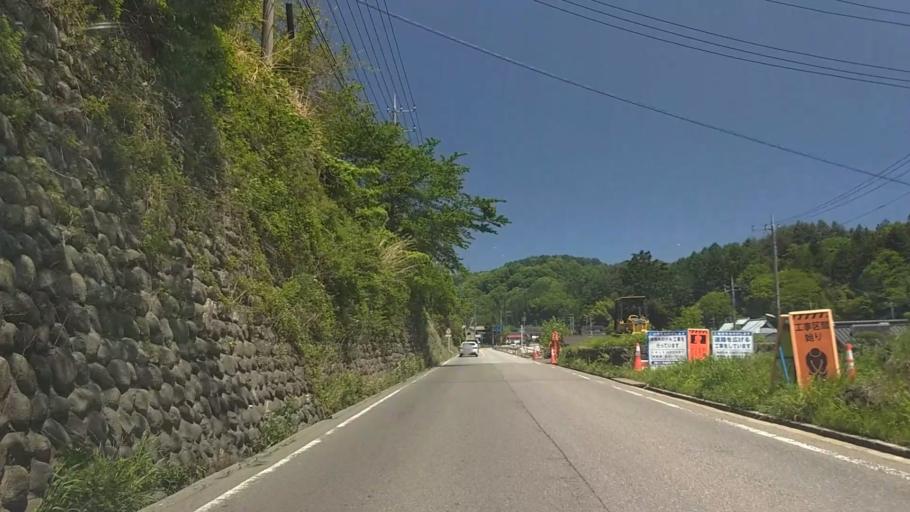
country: JP
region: Yamanashi
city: Nirasaki
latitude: 35.8692
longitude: 138.4273
